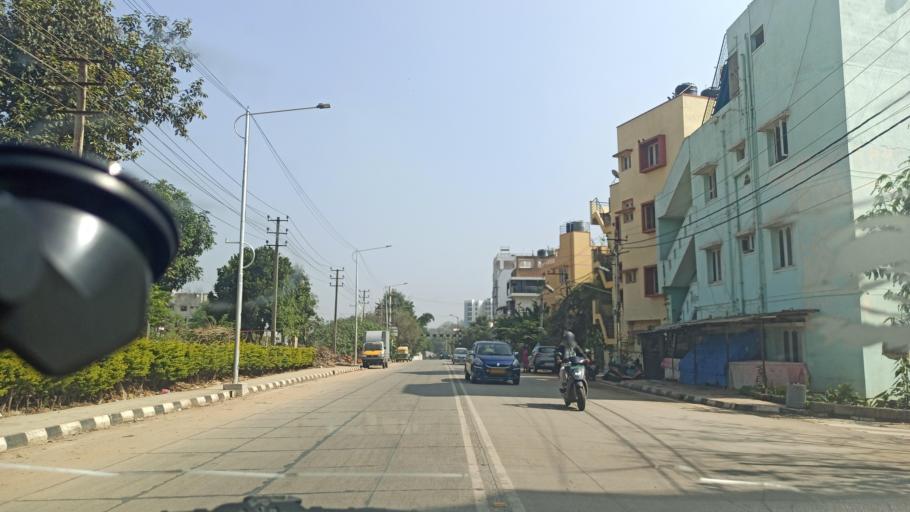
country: IN
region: Karnataka
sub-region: Bangalore Urban
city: Yelahanka
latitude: 13.0679
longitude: 77.5836
